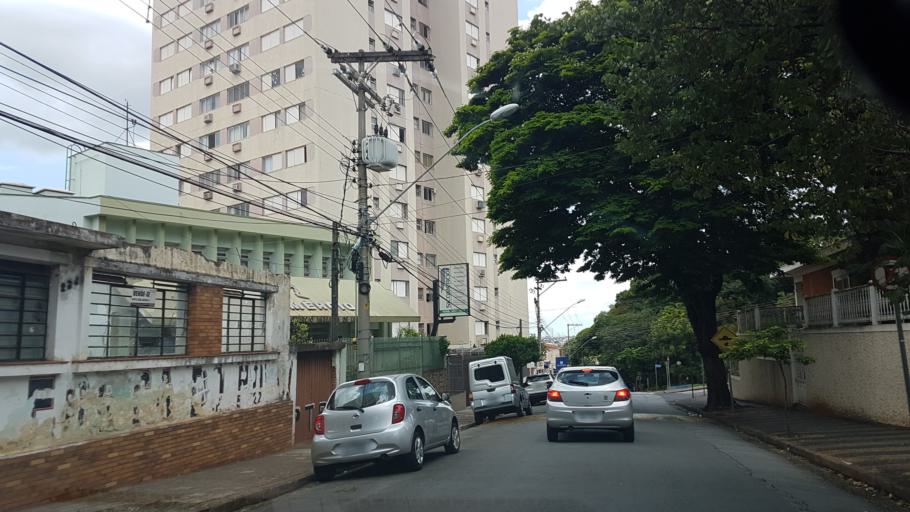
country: BR
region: Sao Paulo
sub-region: Limeira
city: Limeira
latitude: -22.5665
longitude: -47.4005
